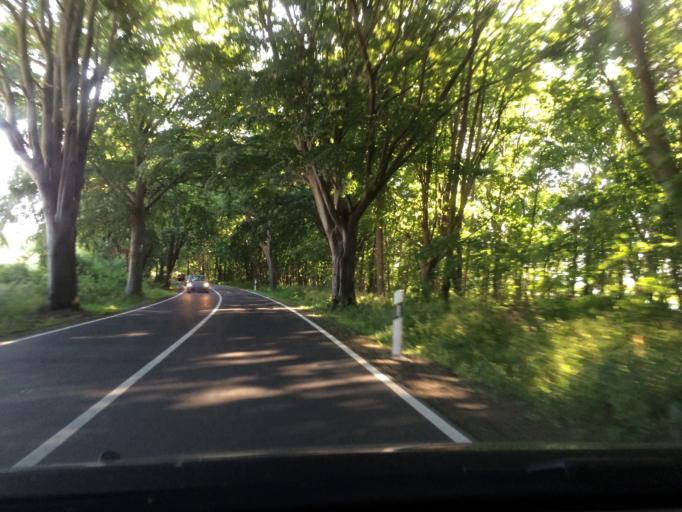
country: DE
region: Mecklenburg-Vorpommern
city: Ostseebad Binz
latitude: 54.4217
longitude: 13.5435
